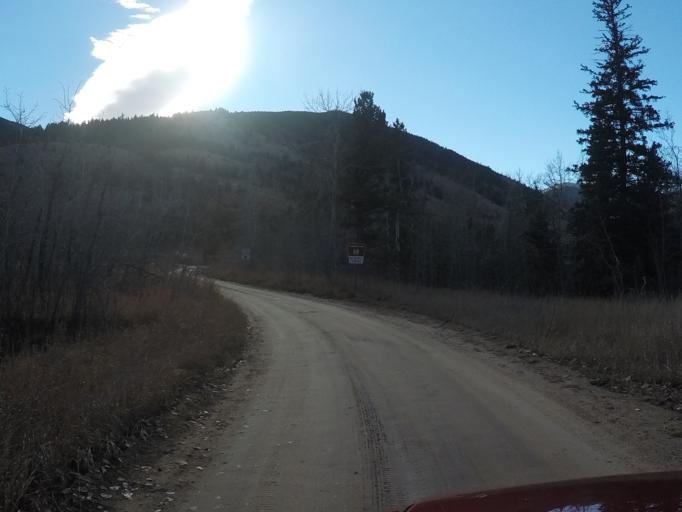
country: US
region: Montana
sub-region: Carbon County
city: Red Lodge
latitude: 45.1157
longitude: -109.2990
